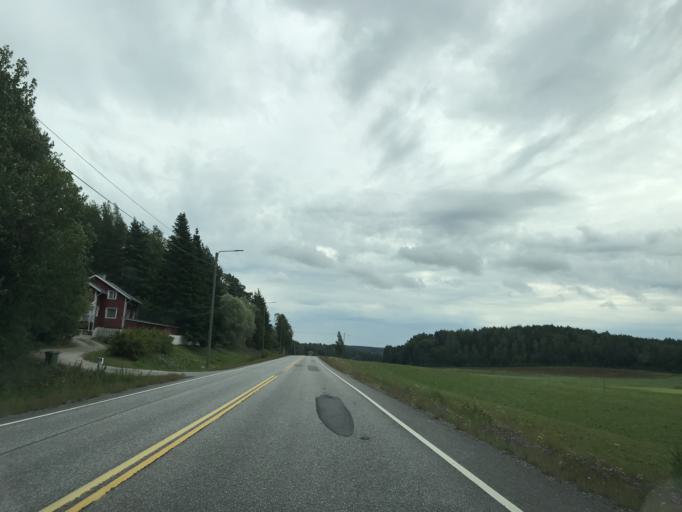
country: FI
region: Varsinais-Suomi
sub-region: Turku
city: Paimio
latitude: 60.4285
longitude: 22.6172
